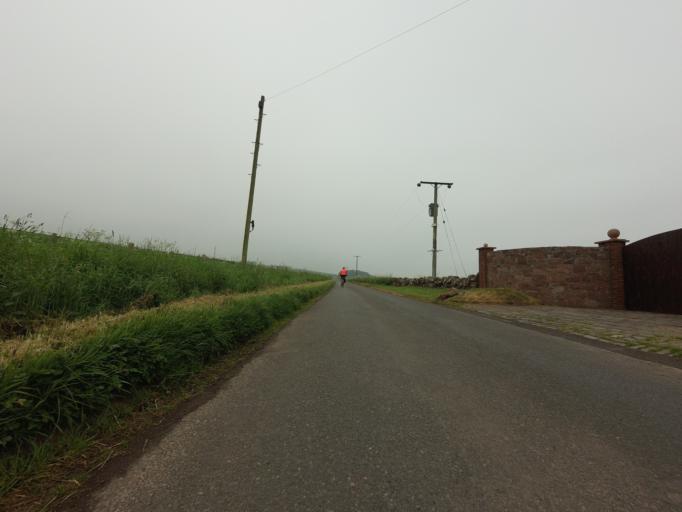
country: GB
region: Scotland
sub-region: Fife
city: Auchtermuchty
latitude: 56.2724
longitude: -3.2811
